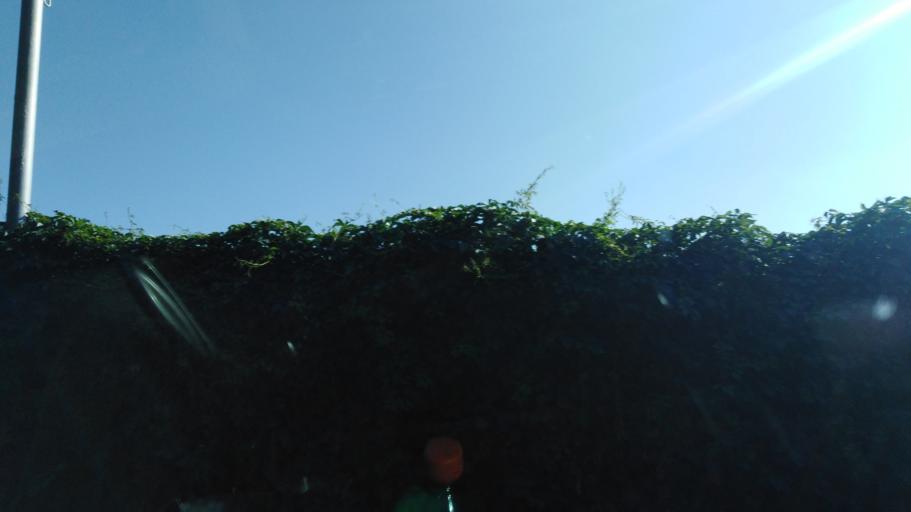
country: RU
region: Stavropol'skiy
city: Svobody
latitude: 44.0389
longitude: 43.0391
